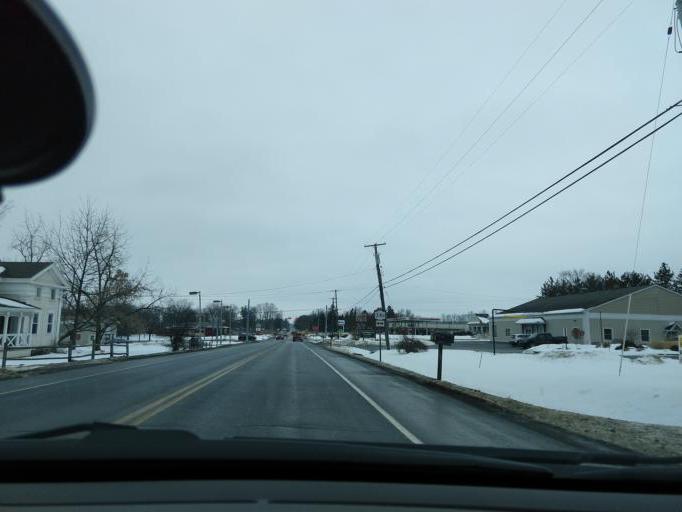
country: US
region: New York
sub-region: Tompkins County
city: Lansing
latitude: 42.5373
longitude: -76.4925
